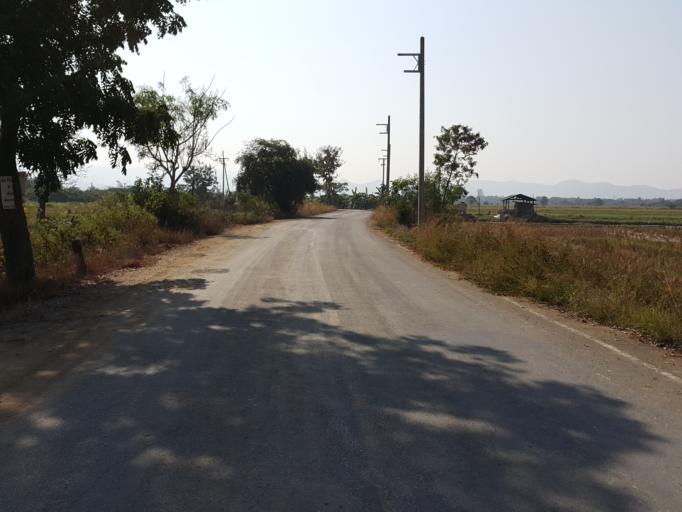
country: TH
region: Lamphun
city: Ban Thi
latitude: 18.6854
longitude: 99.1344
